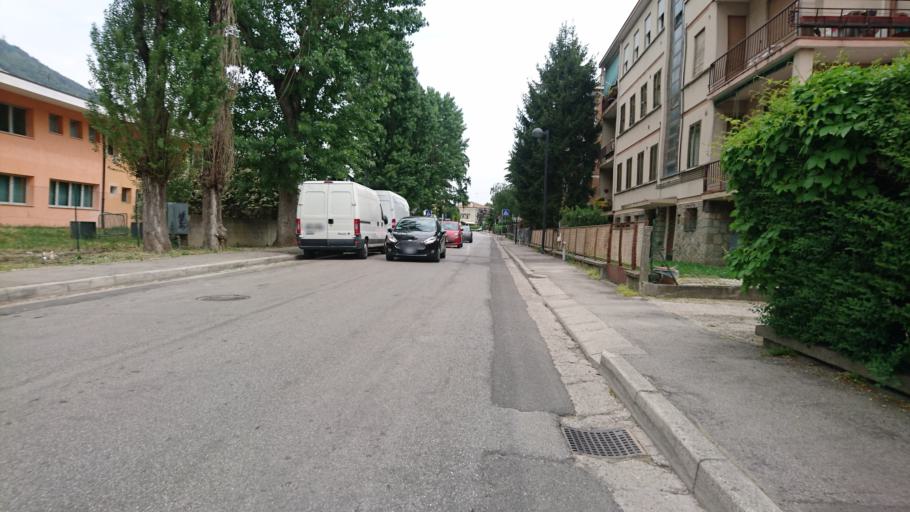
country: IT
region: Veneto
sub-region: Provincia di Padova
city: Monselice
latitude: 45.2428
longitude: 11.7470
